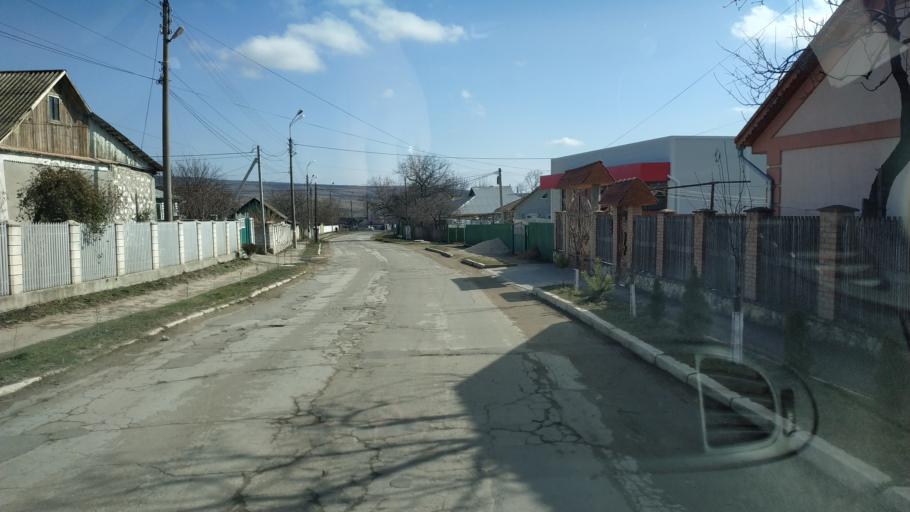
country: MD
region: Hincesti
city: Hincesti
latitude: 46.9719
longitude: 28.5819
